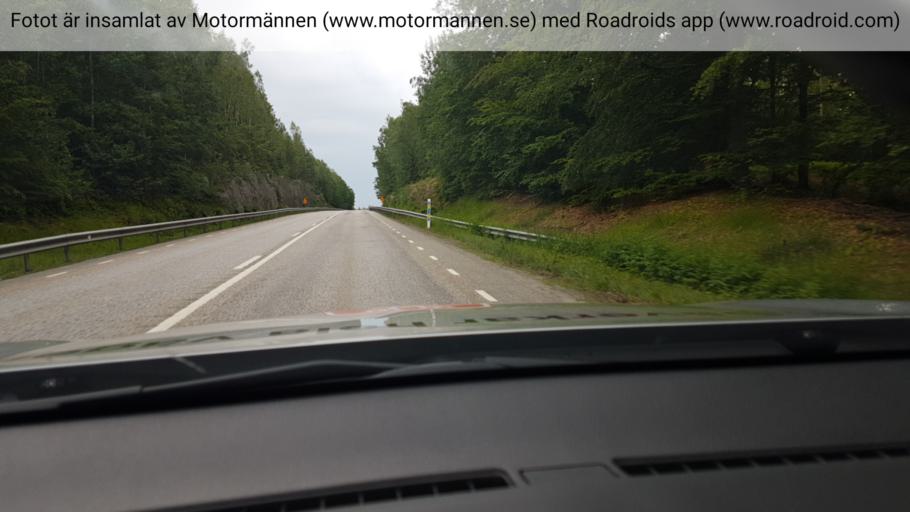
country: SE
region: Joenkoeping
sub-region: Habo Kommun
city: Habo
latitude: 57.9058
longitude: 14.1040
